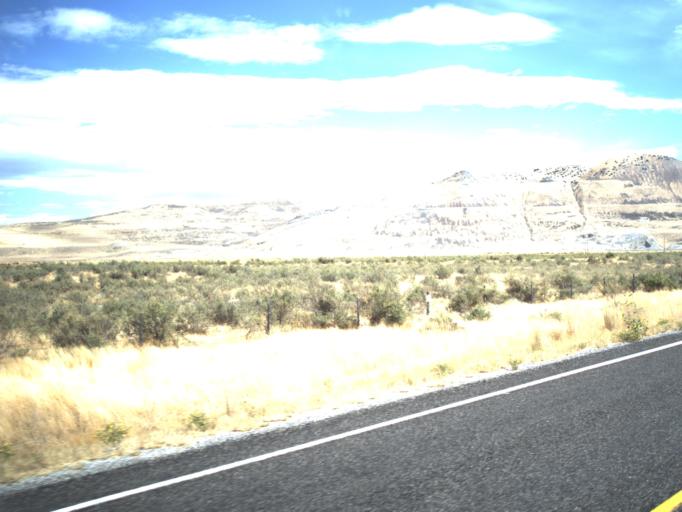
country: US
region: Utah
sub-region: Box Elder County
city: Tremonton
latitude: 41.5990
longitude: -112.2990
